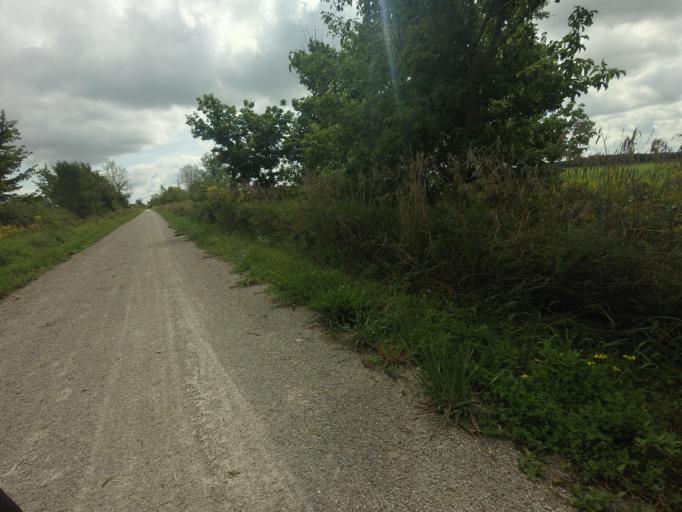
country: CA
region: Ontario
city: North Perth
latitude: 43.5848
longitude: -81.0686
